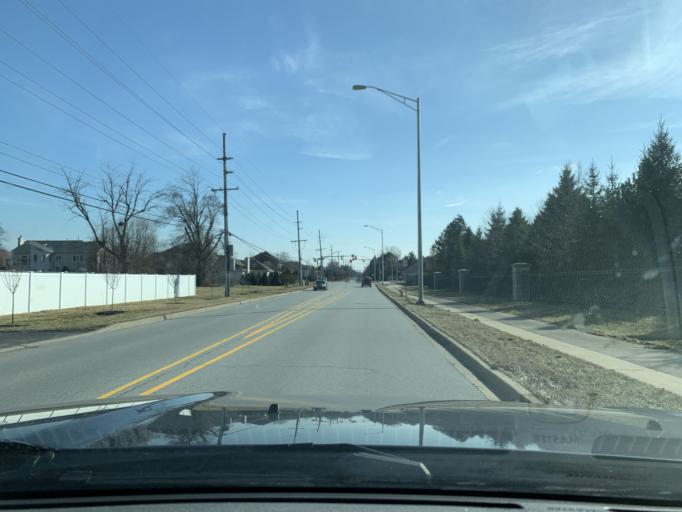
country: US
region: Indiana
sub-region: Lake County
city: Munster
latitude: 41.5322
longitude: -87.4904
